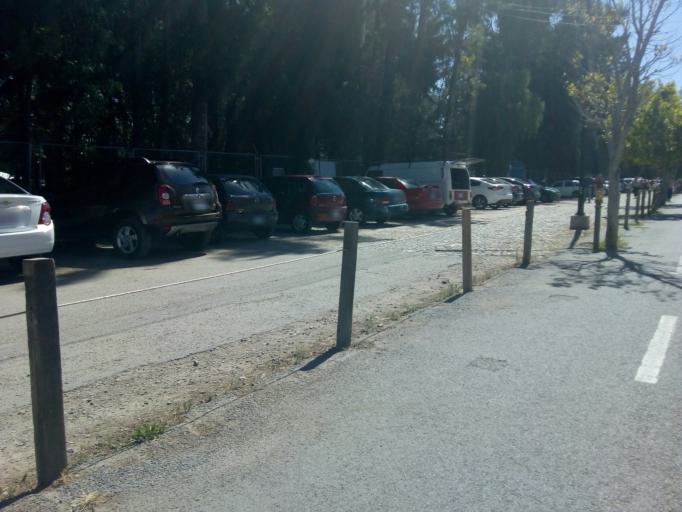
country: MX
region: Guanajuato
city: Leon
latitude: 21.1729
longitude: -101.6876
